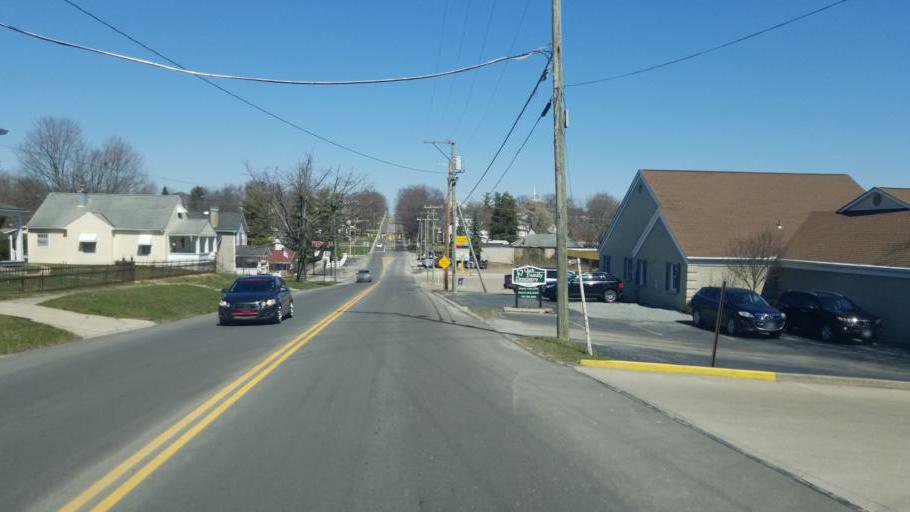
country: US
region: Ohio
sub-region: Highland County
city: Hillsboro
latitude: 39.1952
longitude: -83.6132
